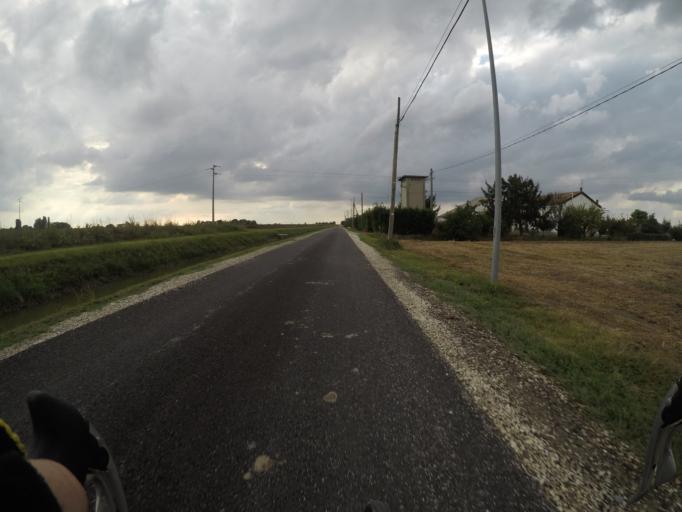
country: IT
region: Veneto
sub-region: Provincia di Rovigo
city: Polesella
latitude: 44.9655
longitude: 11.7357
